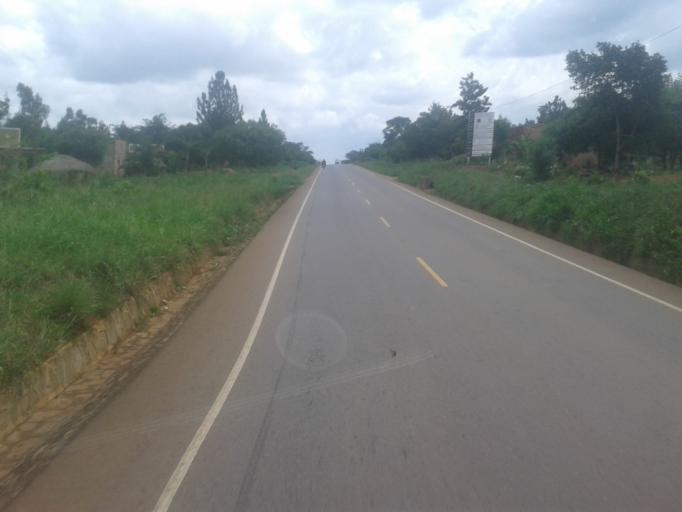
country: UG
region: Central Region
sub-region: Nakasongola District
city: Nakasongola
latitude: 1.1137
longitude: 32.4656
